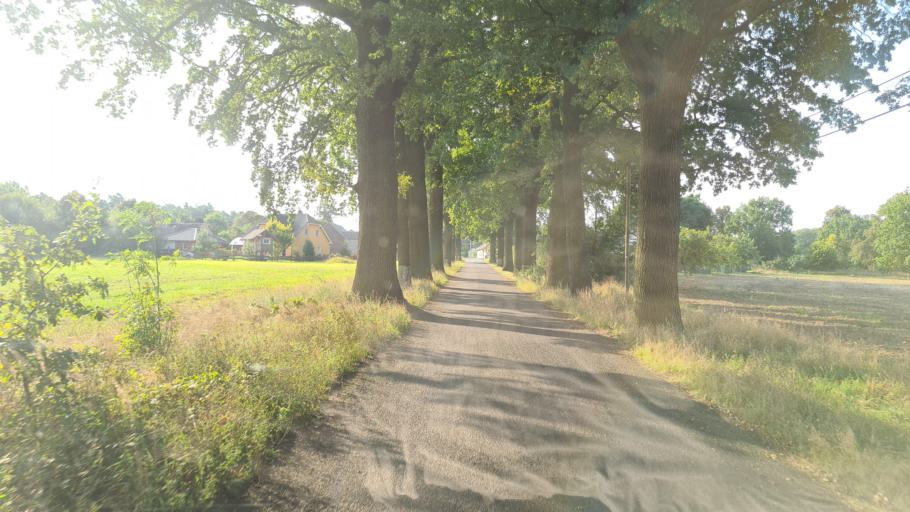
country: DE
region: Brandenburg
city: Neupetershain
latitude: 51.6222
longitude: 14.1046
